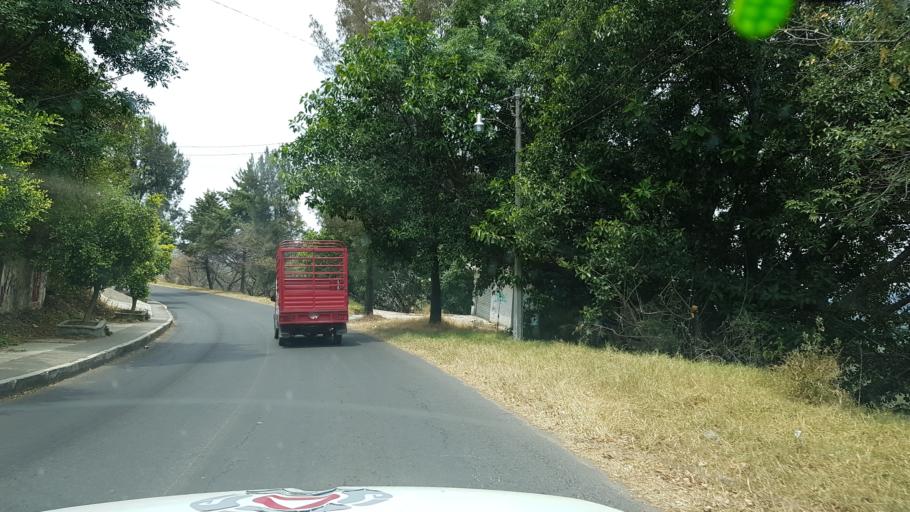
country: MX
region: Morelos
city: Ocuituco
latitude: 18.8814
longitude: -98.7765
